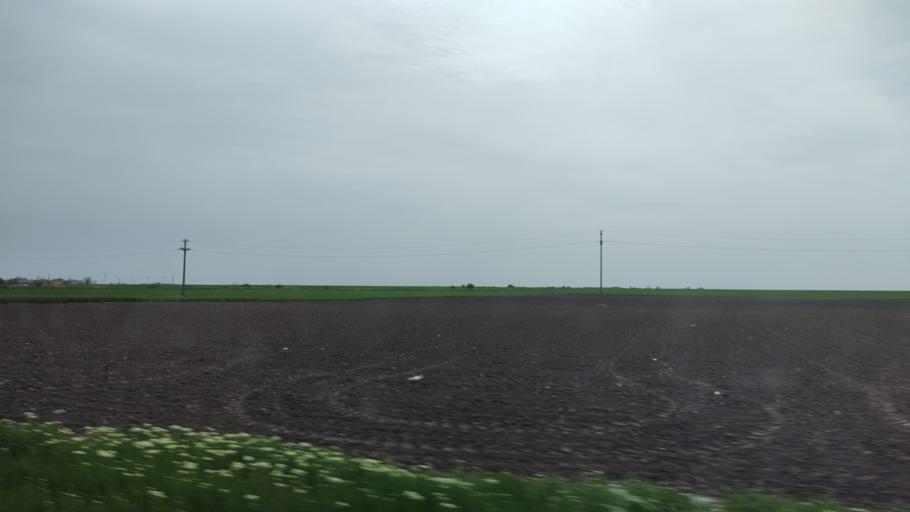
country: RO
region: Constanta
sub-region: Comuna Ciocarlia
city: Ciocarlia de Sus
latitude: 44.1145
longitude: 28.3184
